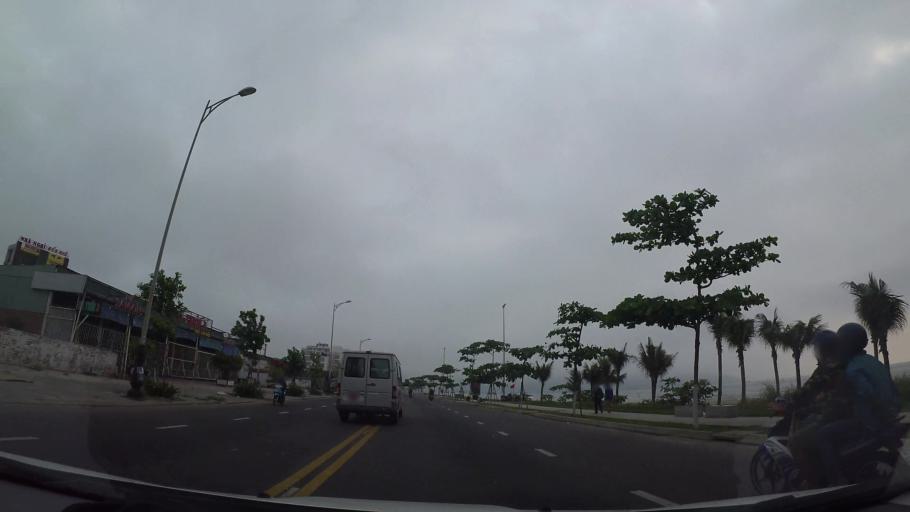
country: VN
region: Da Nang
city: Son Tra
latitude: 16.0814
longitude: 108.2474
